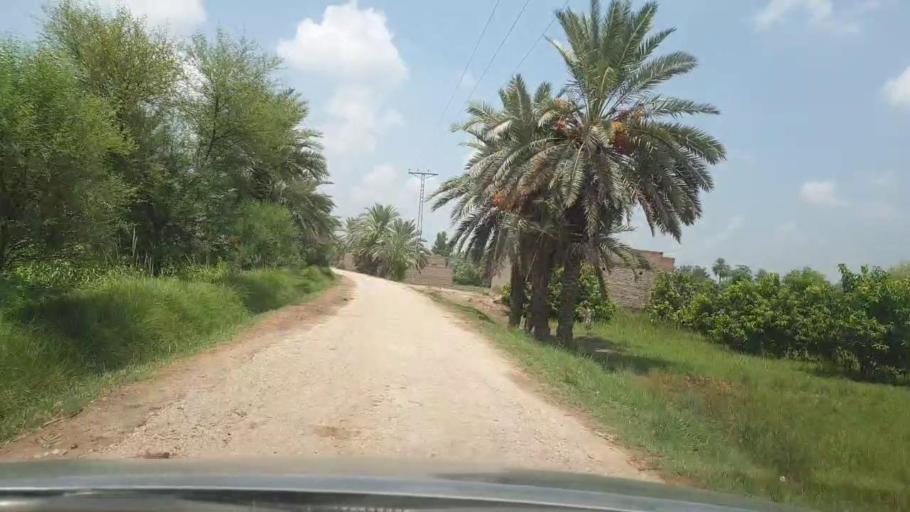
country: PK
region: Sindh
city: Pir jo Goth
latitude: 27.6067
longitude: 68.6133
